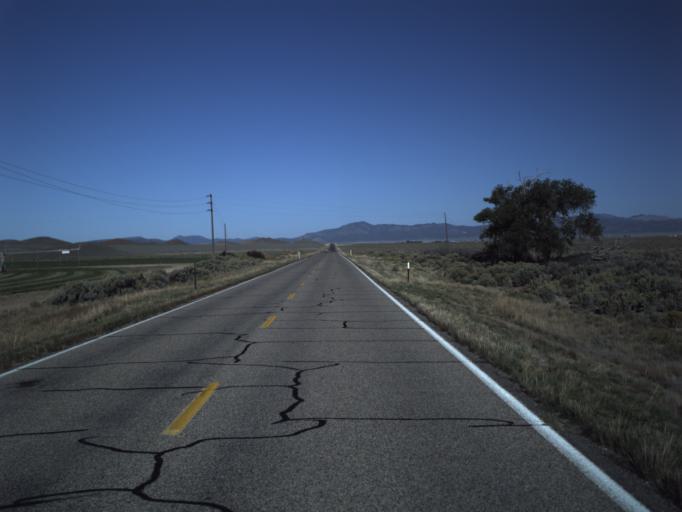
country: US
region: Utah
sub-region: Washington County
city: Enterprise
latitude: 37.7252
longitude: -113.6999
